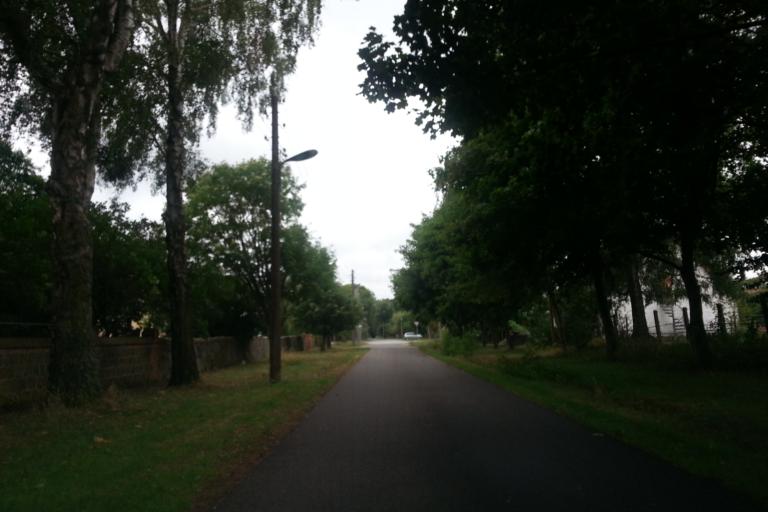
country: DE
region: Mecklenburg-Vorpommern
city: Ferdinandshof
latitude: 53.6888
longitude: 13.9004
